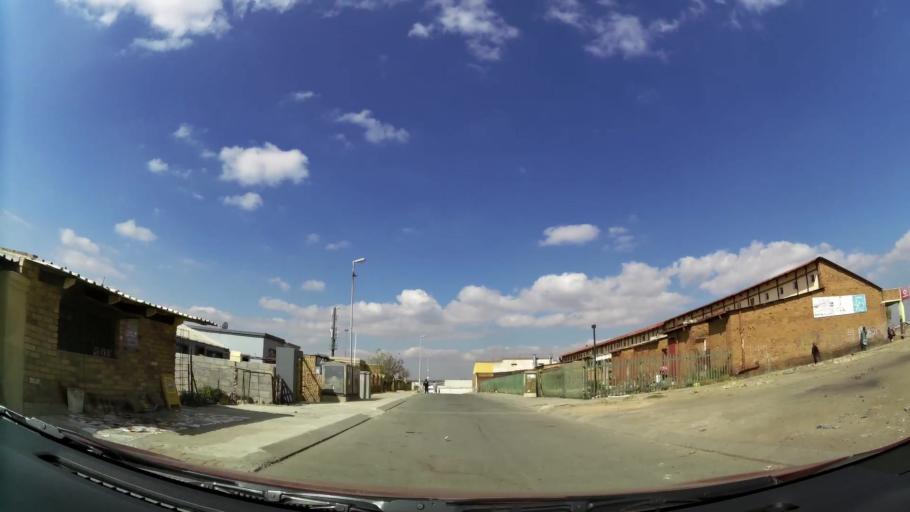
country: ZA
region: Gauteng
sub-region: Ekurhuleni Metropolitan Municipality
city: Tembisa
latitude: -26.0197
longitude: 28.1919
